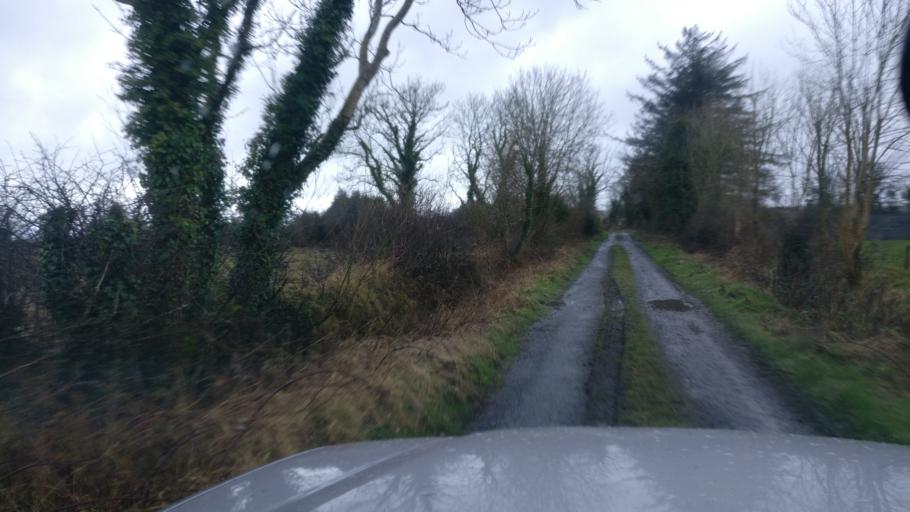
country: IE
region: Connaught
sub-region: County Galway
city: Ballinasloe
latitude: 53.2515
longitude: -8.3326
